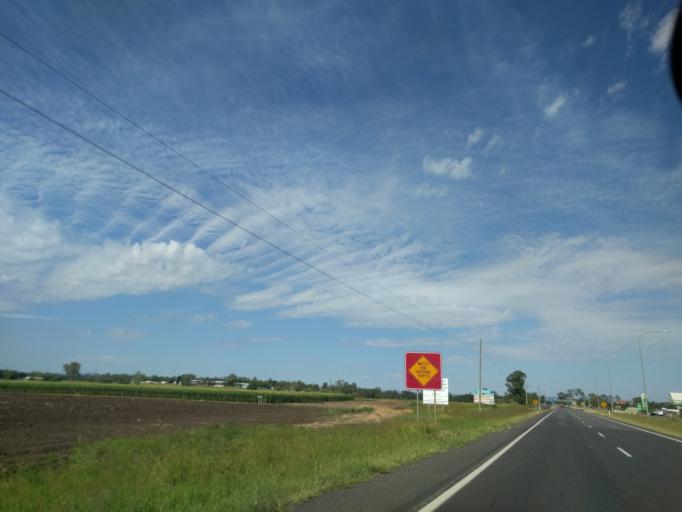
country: AU
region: Queensland
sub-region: Lockyer Valley
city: Gatton
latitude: -27.5445
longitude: 152.3474
